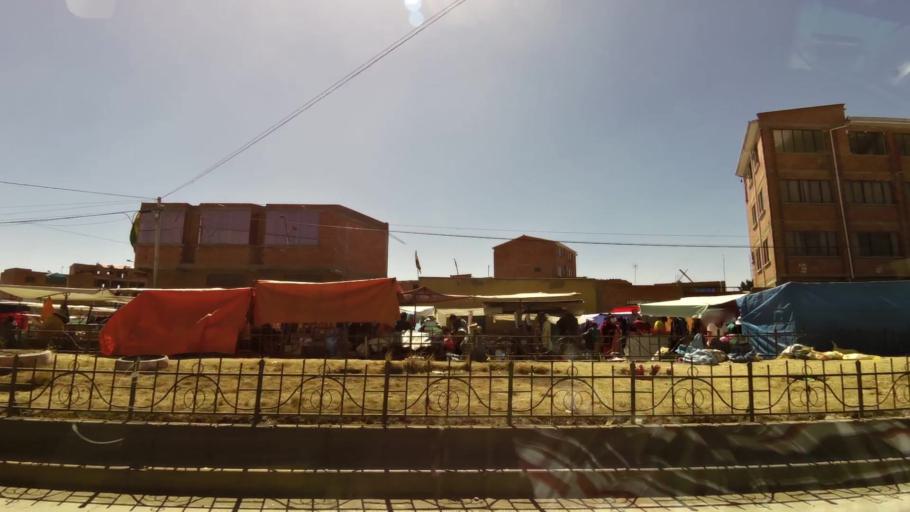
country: BO
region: La Paz
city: La Paz
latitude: -16.5017
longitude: -68.2251
